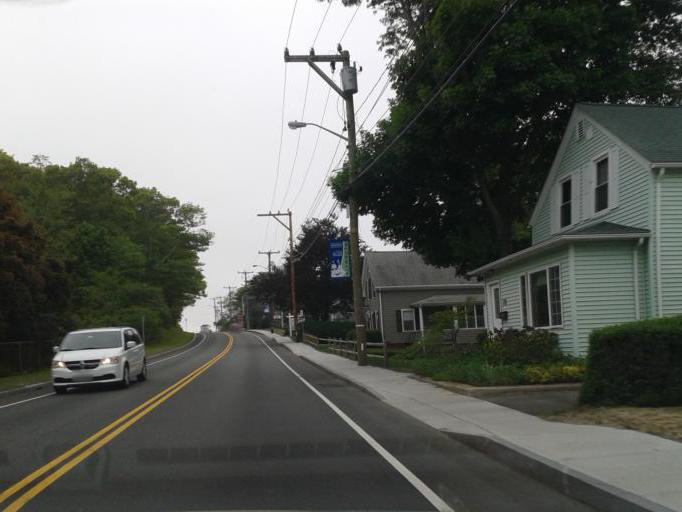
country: US
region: Massachusetts
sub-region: Plymouth County
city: Plymouth
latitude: 41.9569
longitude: -70.6764
